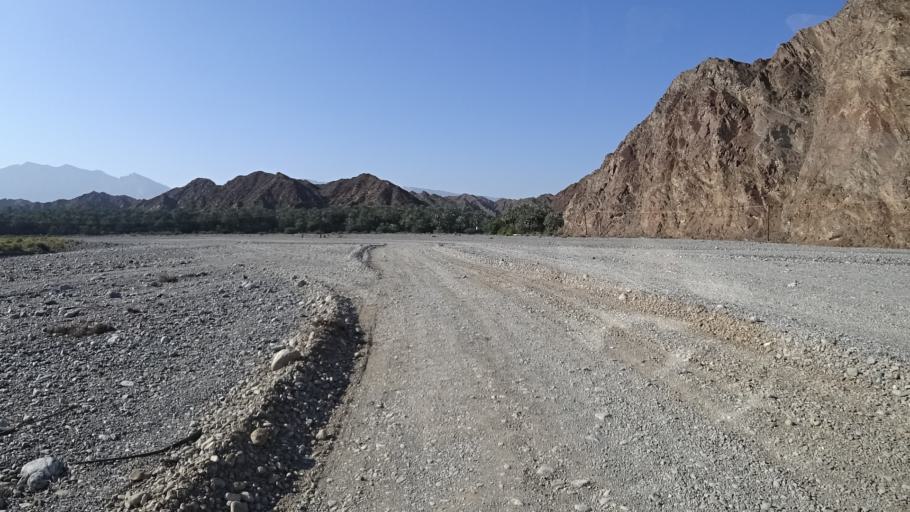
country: OM
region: Al Batinah
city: Bayt al `Awabi
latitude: 23.3887
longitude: 57.6595
